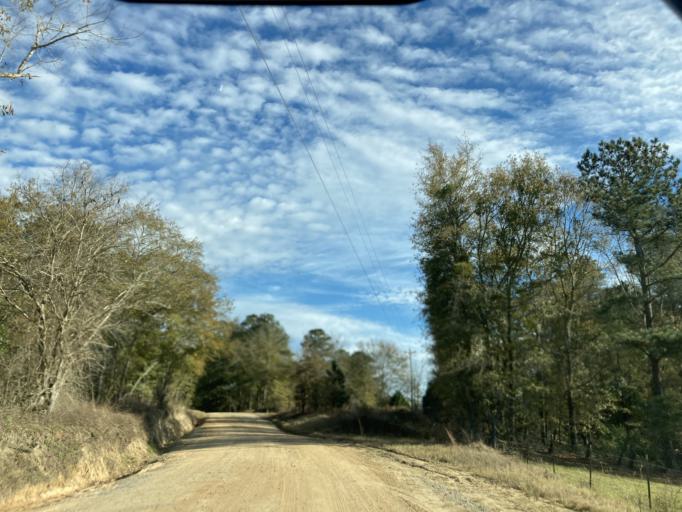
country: US
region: Georgia
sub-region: Jones County
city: Gray
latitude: 32.9116
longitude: -83.4977
